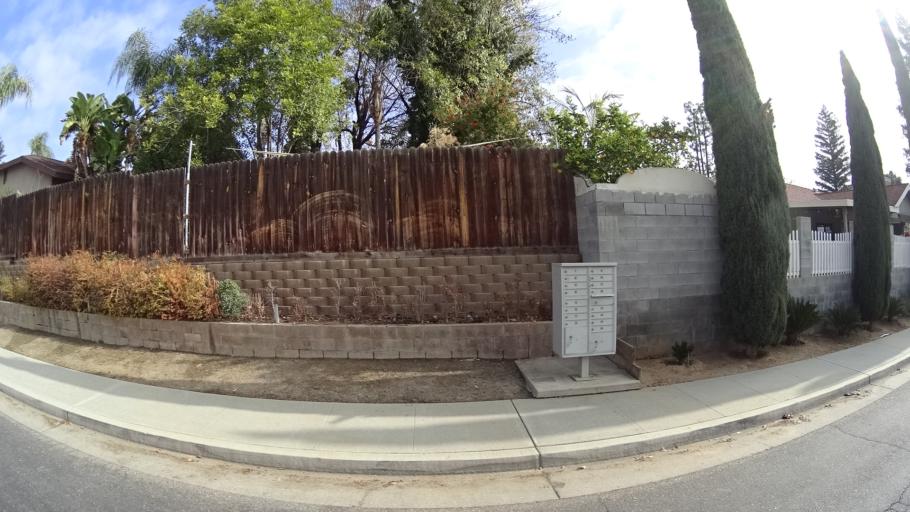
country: US
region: California
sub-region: Kern County
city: Bakersfield
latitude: 35.3898
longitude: -118.9277
